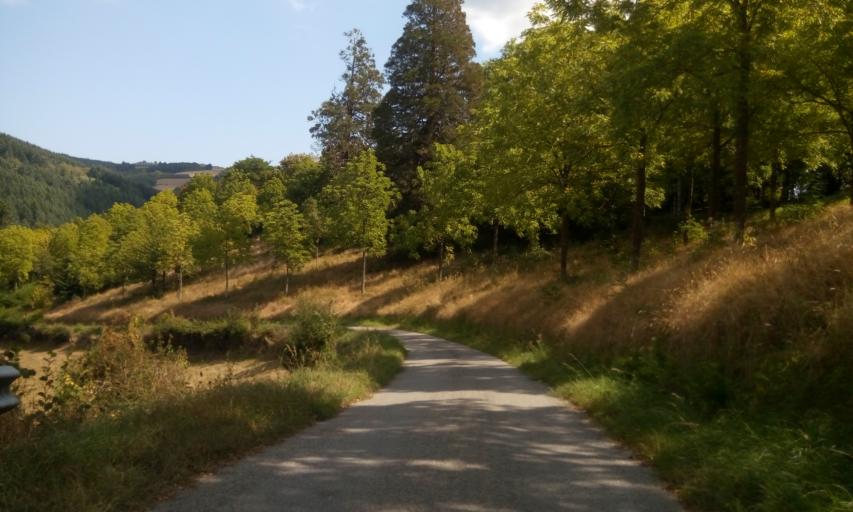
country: FR
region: Rhone-Alpes
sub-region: Departement du Rhone
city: Grandris
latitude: 46.0075
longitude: 4.4913
